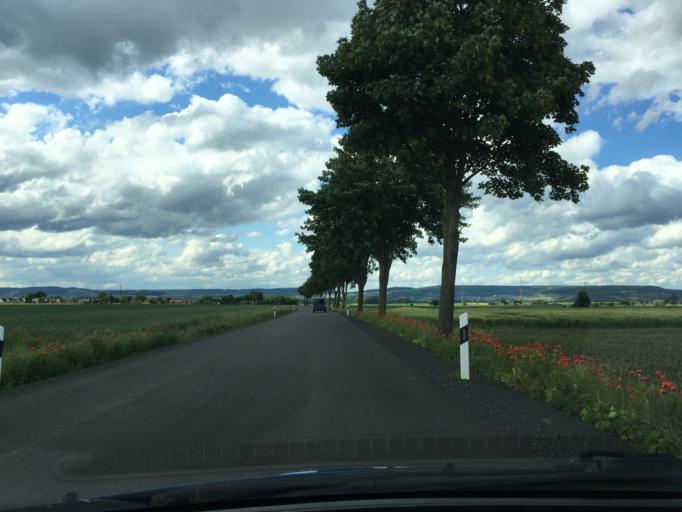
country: DE
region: Lower Saxony
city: Moringen
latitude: 51.7569
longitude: 9.8726
